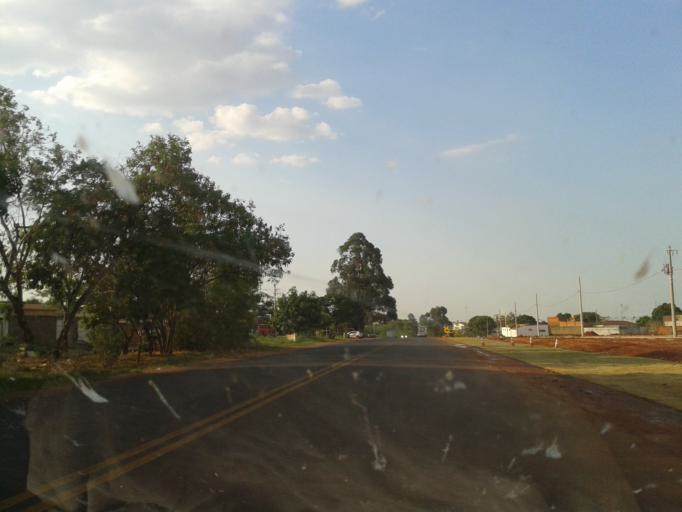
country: BR
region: Minas Gerais
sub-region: Uberlandia
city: Uberlandia
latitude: -18.9581
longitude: -48.3068
